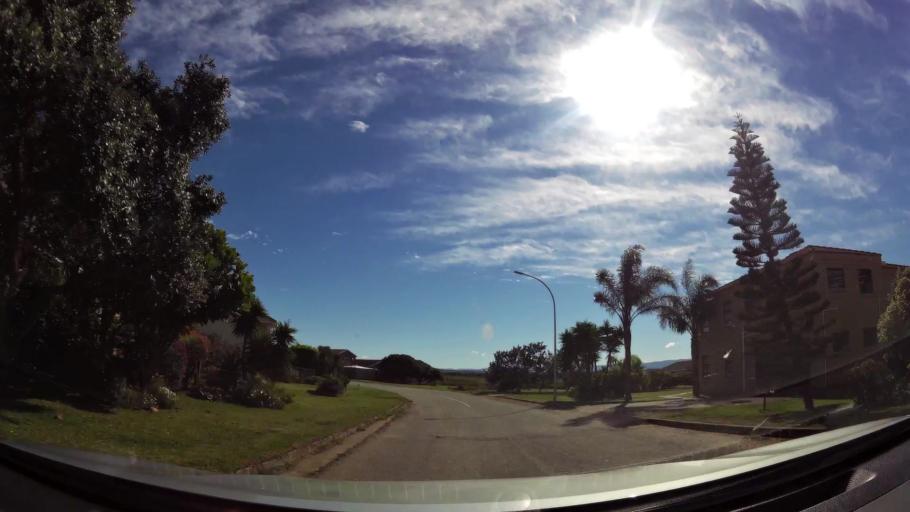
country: ZA
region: Eastern Cape
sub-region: Cacadu District Municipality
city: Jeffrey's Bay
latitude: -34.0160
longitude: 24.9252
